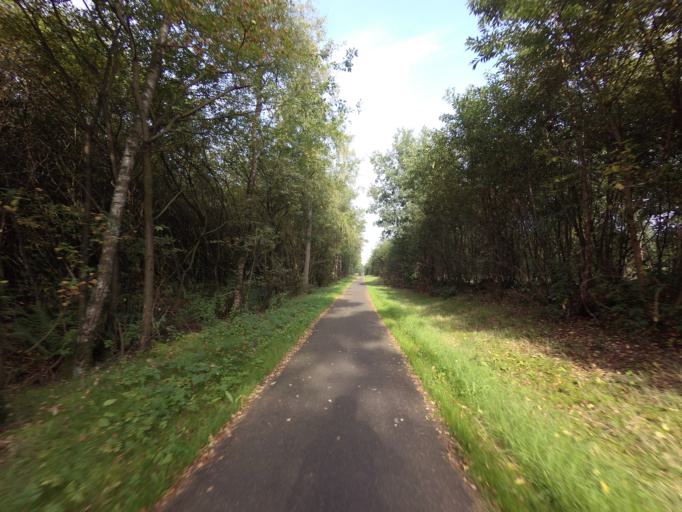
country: DE
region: Lower Saxony
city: Wielen
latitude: 52.5241
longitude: 6.7386
